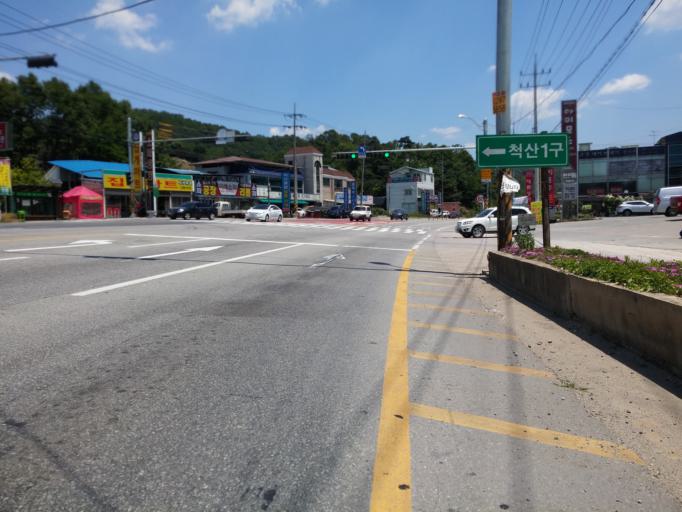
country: KR
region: Chungcheongbuk-do
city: Cheongju-si
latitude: 36.5626
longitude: 127.4397
